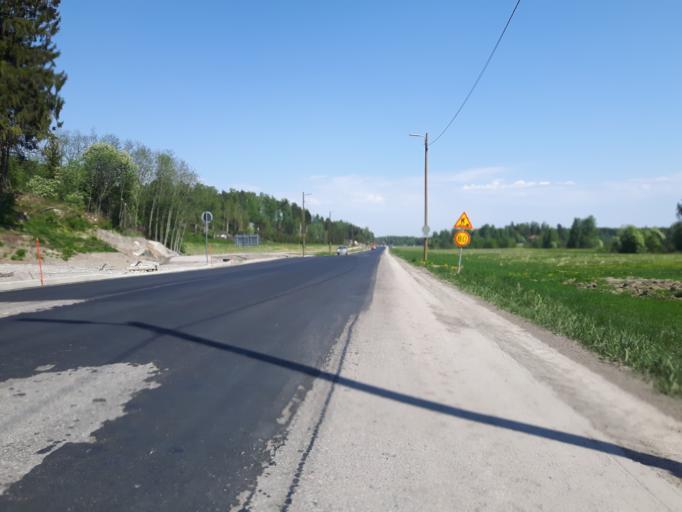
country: FI
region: Uusimaa
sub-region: Helsinki
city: Pornainen
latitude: 60.3441
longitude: 25.4841
